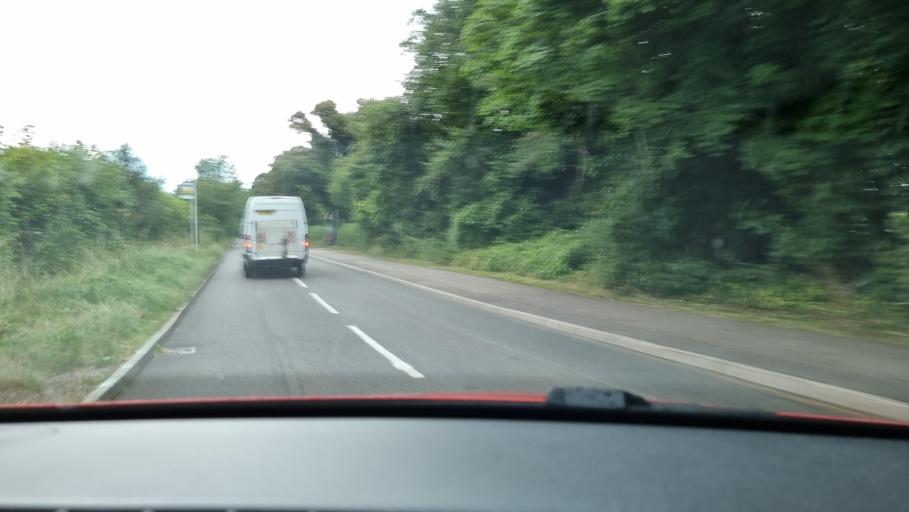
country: GB
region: England
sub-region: Hertfordshire
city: Tring
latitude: 51.7920
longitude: -0.6392
